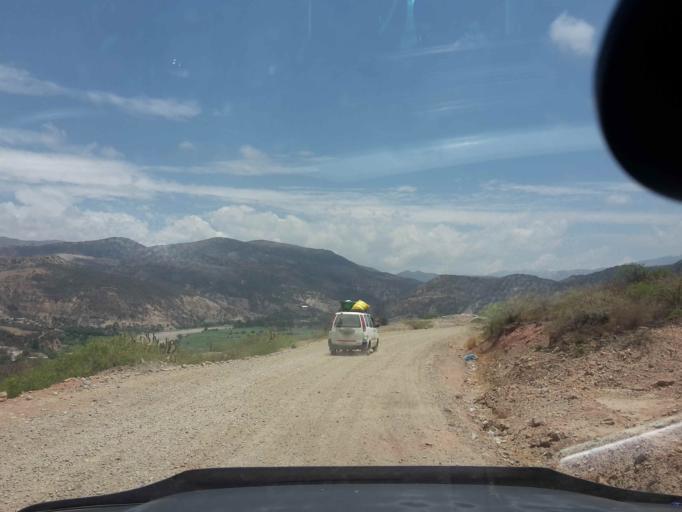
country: BO
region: Cochabamba
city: Sipe Sipe
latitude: -17.5707
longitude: -66.3490
